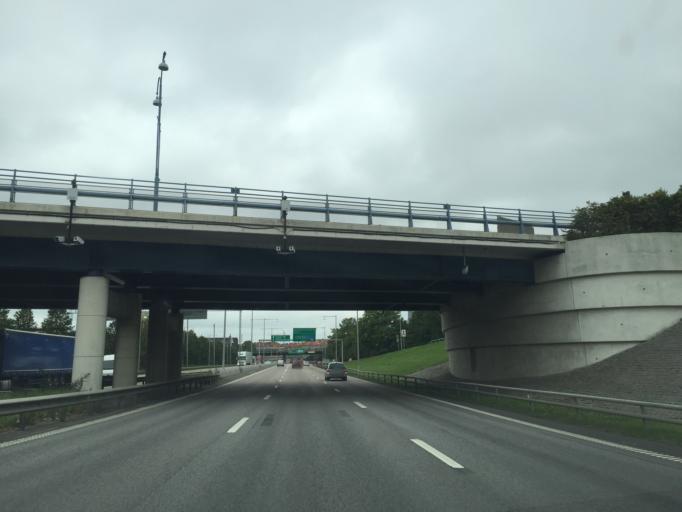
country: SE
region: Vaestra Goetaland
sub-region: Goteborg
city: Goeteborg
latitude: 57.7062
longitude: 11.9958
